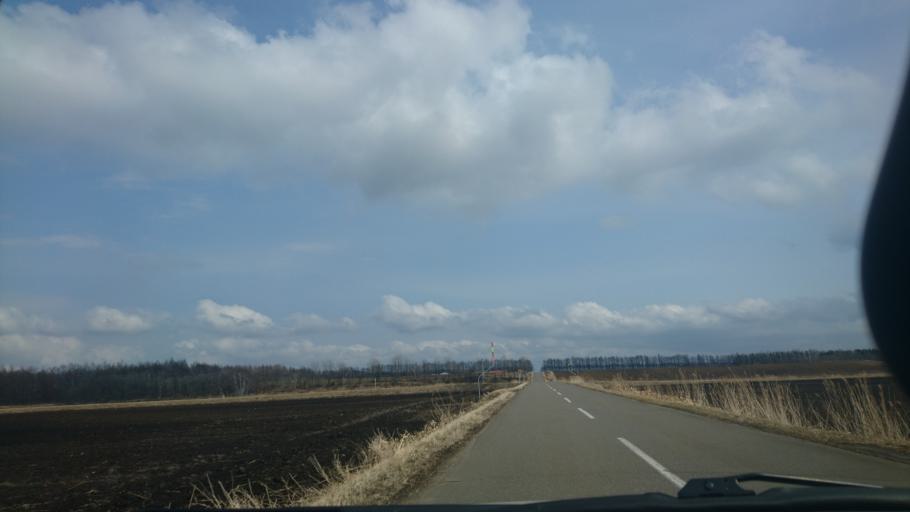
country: JP
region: Hokkaido
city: Otofuke
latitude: 43.2054
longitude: 143.2871
